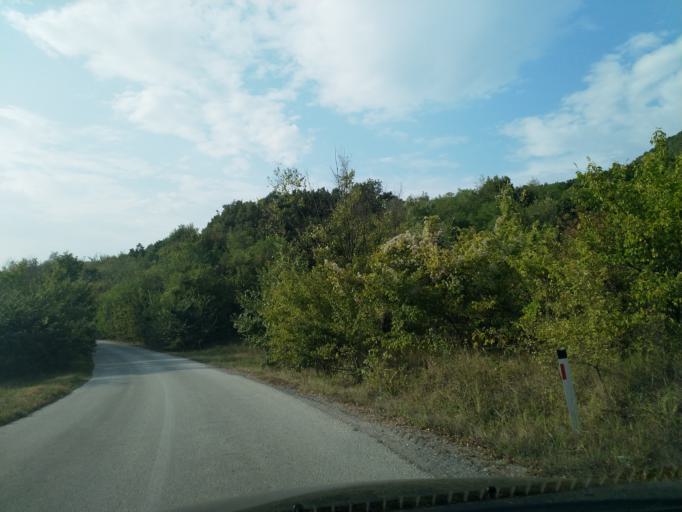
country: RS
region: Central Serbia
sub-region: Pomoravski Okrug
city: Paracin
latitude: 43.8403
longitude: 21.5385
